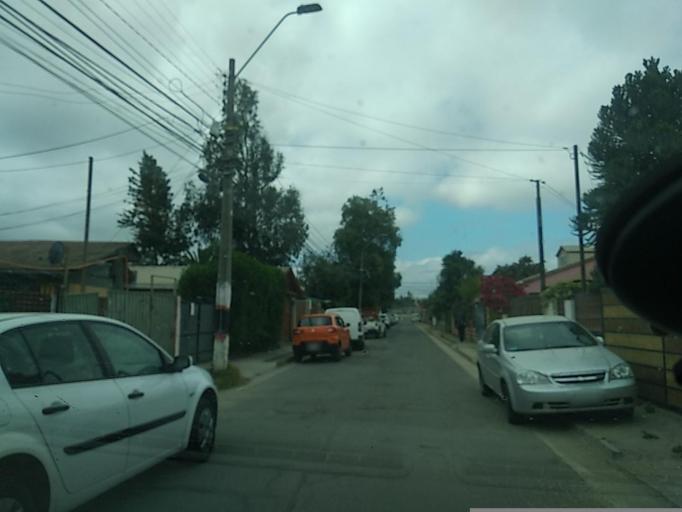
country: CL
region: Valparaiso
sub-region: Provincia de Marga Marga
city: Villa Alemana
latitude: -33.0400
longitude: -71.3591
